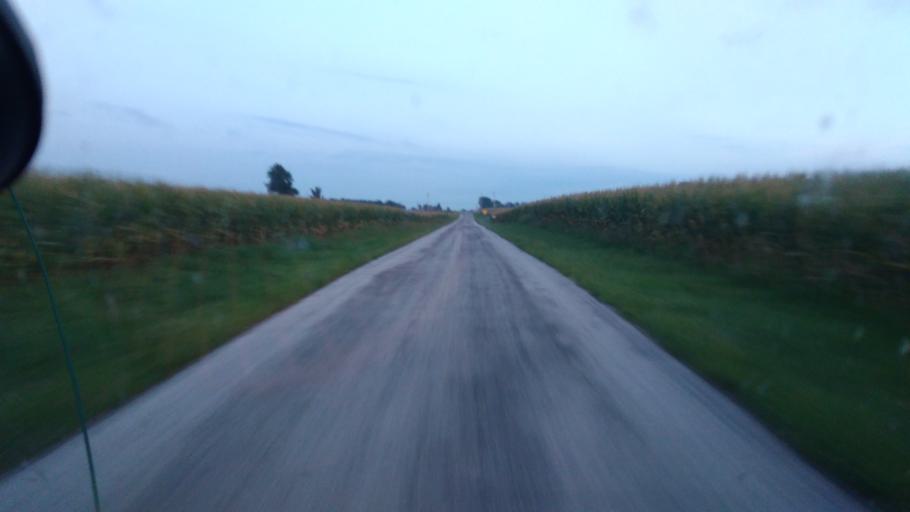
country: US
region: Ohio
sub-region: Hardin County
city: Kenton
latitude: 40.6468
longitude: -83.4582
